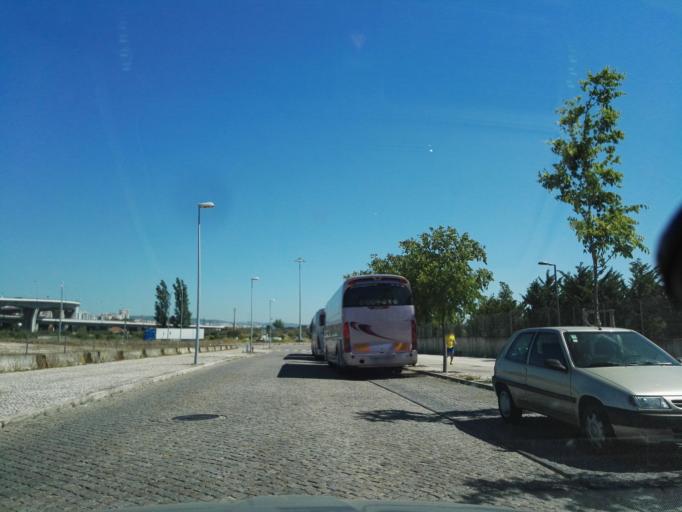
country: PT
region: Lisbon
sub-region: Loures
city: Sacavem
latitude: 38.7945
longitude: -9.0973
